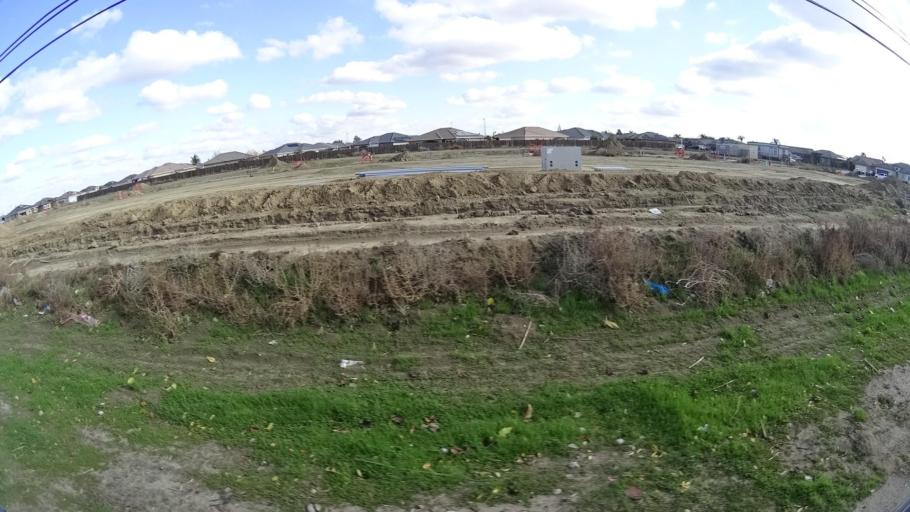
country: US
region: California
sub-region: Kern County
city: McFarland
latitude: 35.6861
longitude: -119.2408
